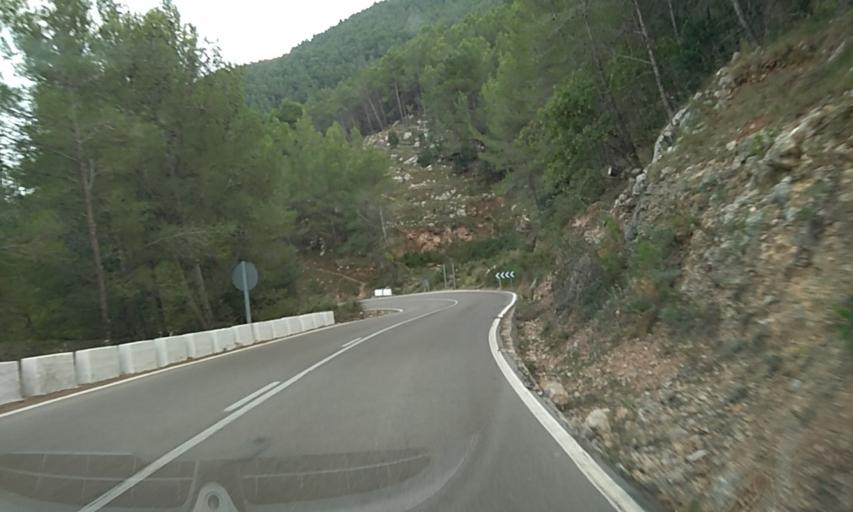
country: ES
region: Valencia
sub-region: Provincia de Castello
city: Montanejos
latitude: 40.0834
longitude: -0.5484
